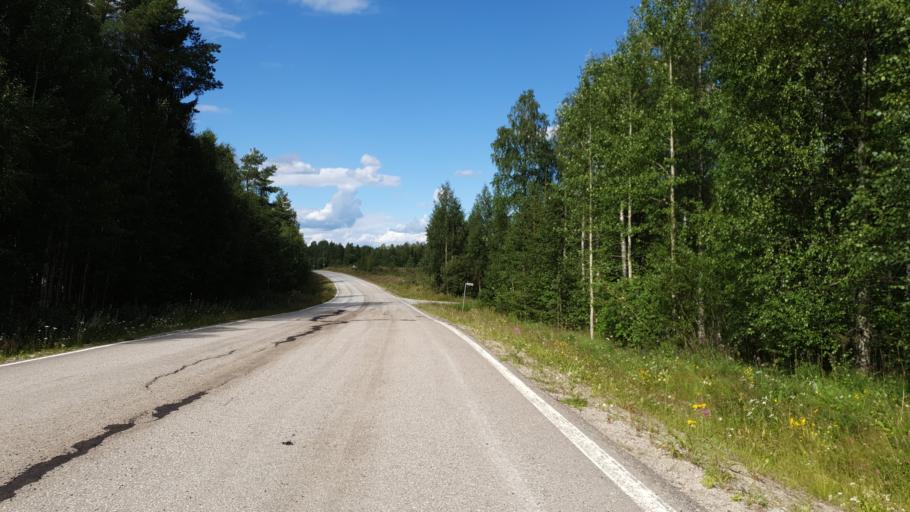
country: FI
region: Kainuu
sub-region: Kehys-Kainuu
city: Kuhmo
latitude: 64.1128
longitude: 29.5277
